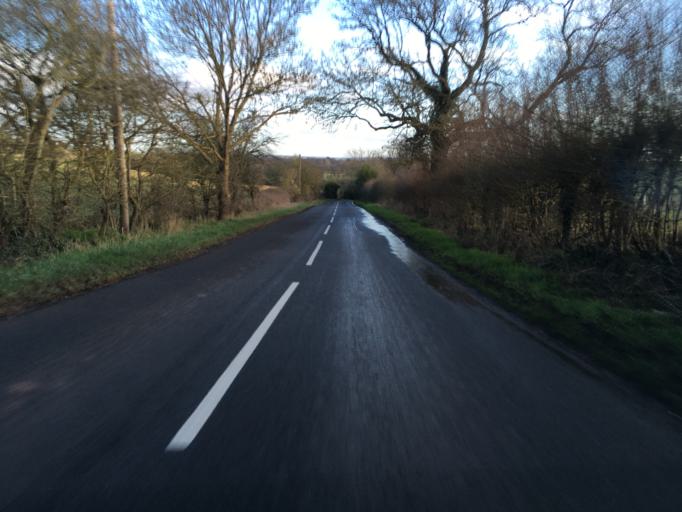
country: GB
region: England
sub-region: Warwickshire
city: Stratford-upon-Avon
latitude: 52.2121
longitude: -1.6834
